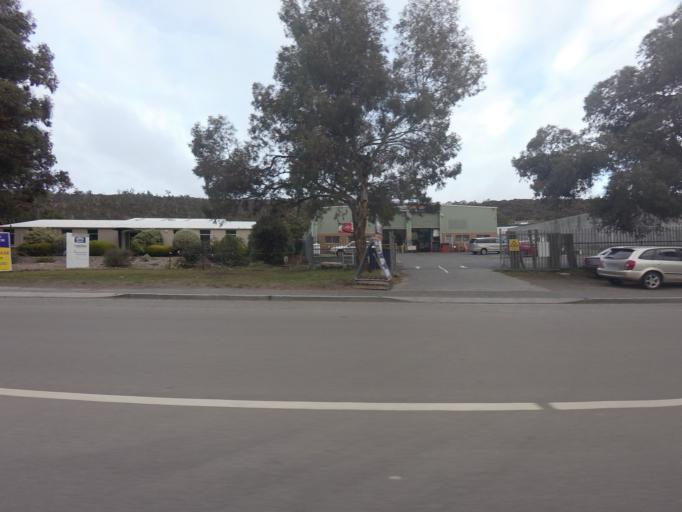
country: AU
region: Tasmania
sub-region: Clarence
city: Warrane
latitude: -42.8613
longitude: 147.4019
